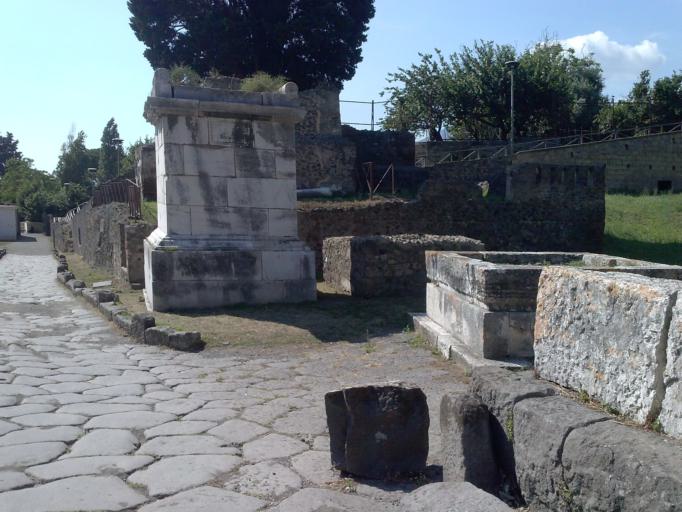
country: IT
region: Campania
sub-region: Provincia di Napoli
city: Pompei
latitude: 40.7524
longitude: 14.4795
